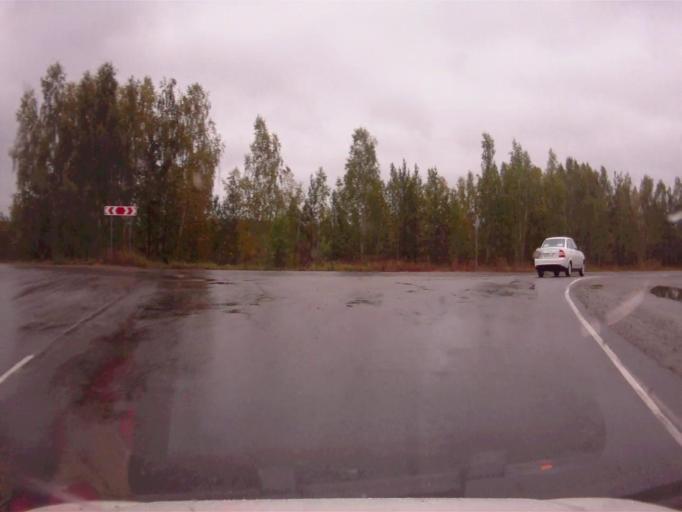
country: RU
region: Chelyabinsk
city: Kyshtym
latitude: 55.7246
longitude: 60.5160
